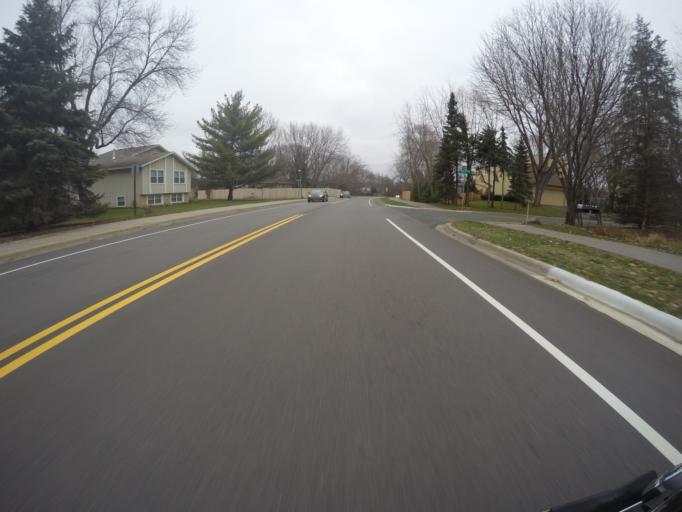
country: US
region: Minnesota
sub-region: Carver County
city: Chanhassen
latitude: 44.8732
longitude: -93.5071
